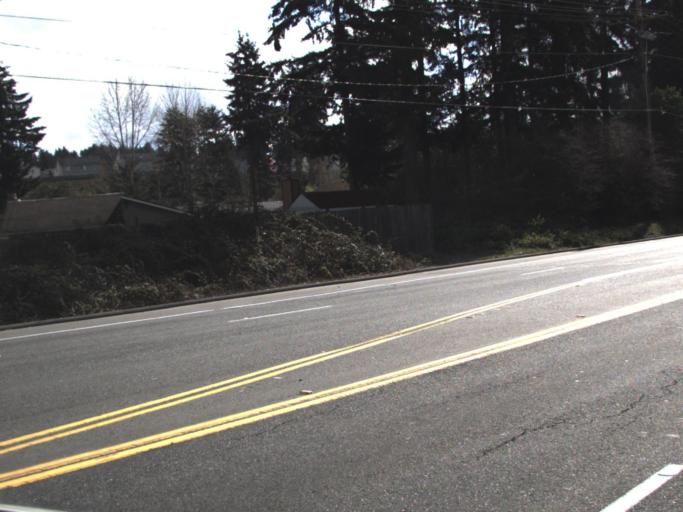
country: US
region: Washington
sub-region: King County
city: Lakeland South
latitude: 47.2771
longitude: -122.3093
